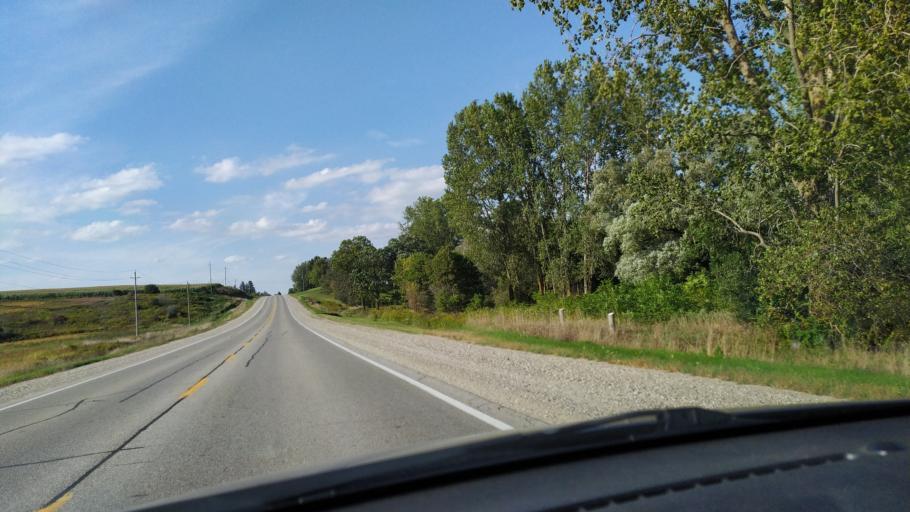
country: CA
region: Ontario
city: Ingersoll
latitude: 43.1399
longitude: -80.8932
